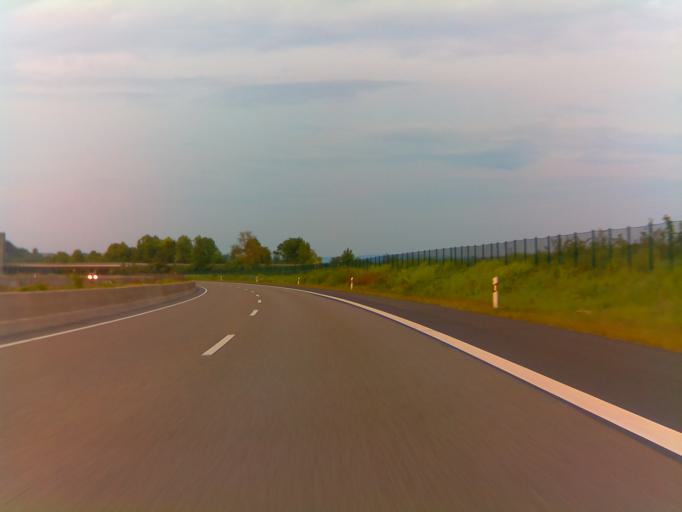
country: DE
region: Hesse
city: Gudensberg
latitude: 51.2020
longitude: 9.4075
